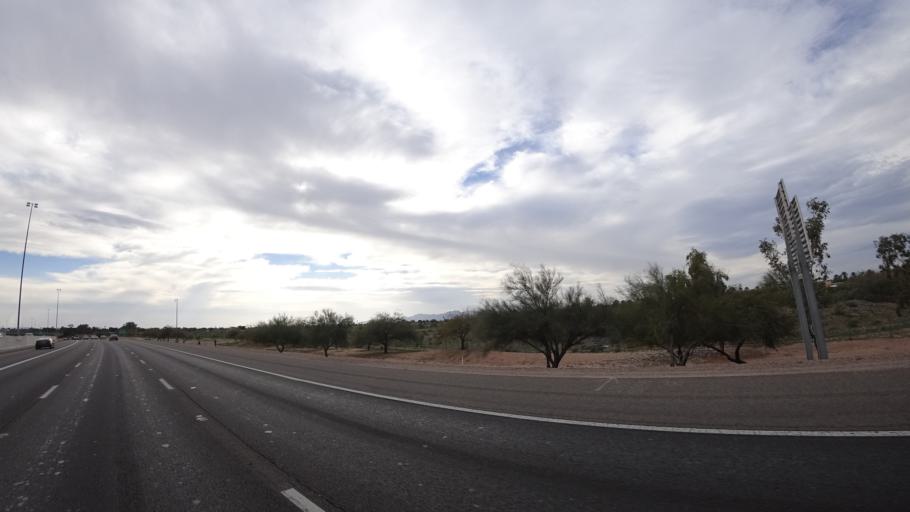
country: US
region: Arizona
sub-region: Maricopa County
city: Sun City
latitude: 33.5990
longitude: -112.2580
